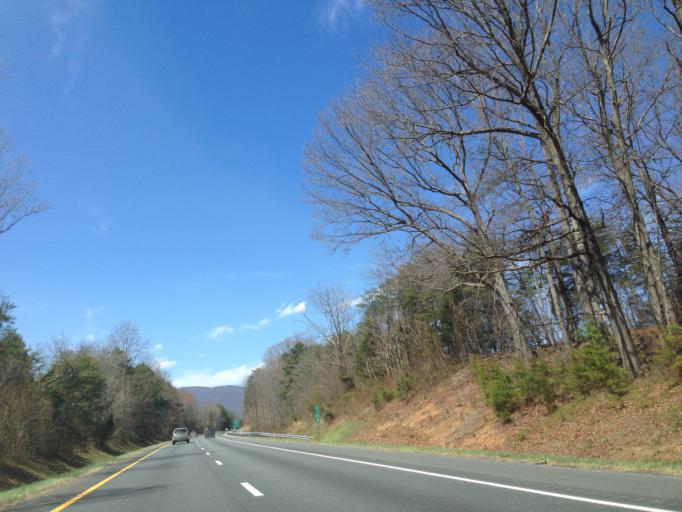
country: US
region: Virginia
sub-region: Albemarle County
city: Crozet
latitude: 38.0409
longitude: -78.7163
